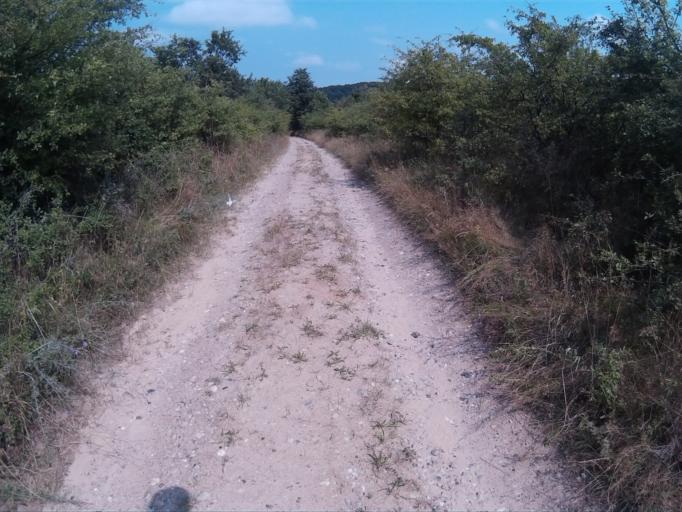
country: HU
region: Veszprem
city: Papa
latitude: 47.2894
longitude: 17.6192
